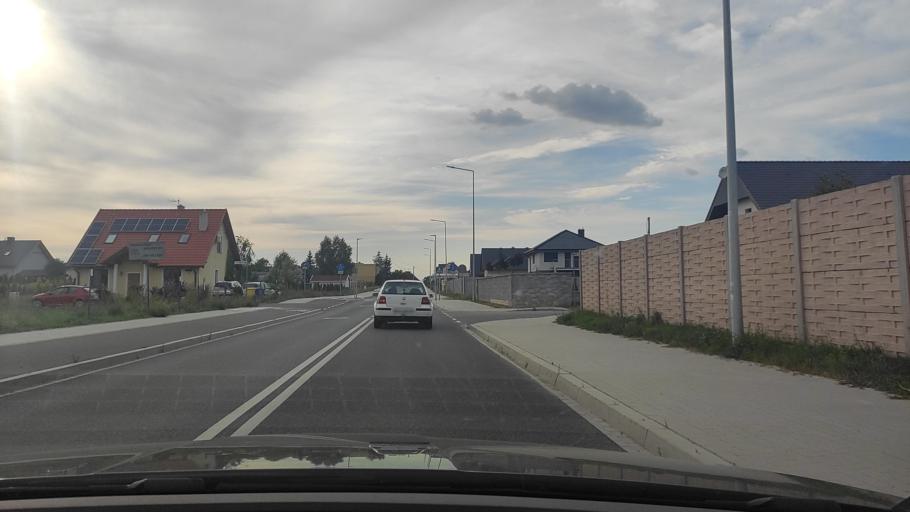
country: PL
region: Greater Poland Voivodeship
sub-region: Powiat poznanski
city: Kornik
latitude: 52.2980
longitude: 17.0941
